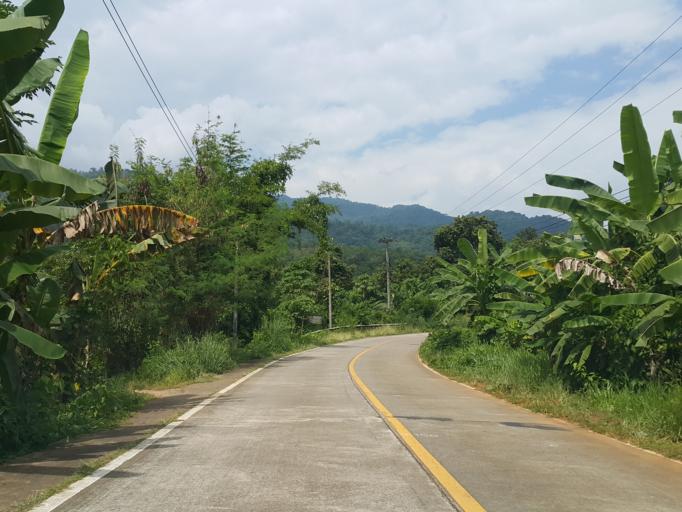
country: TH
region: Mae Hong Son
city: Mae Hong Son
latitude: 19.4500
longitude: 97.9655
